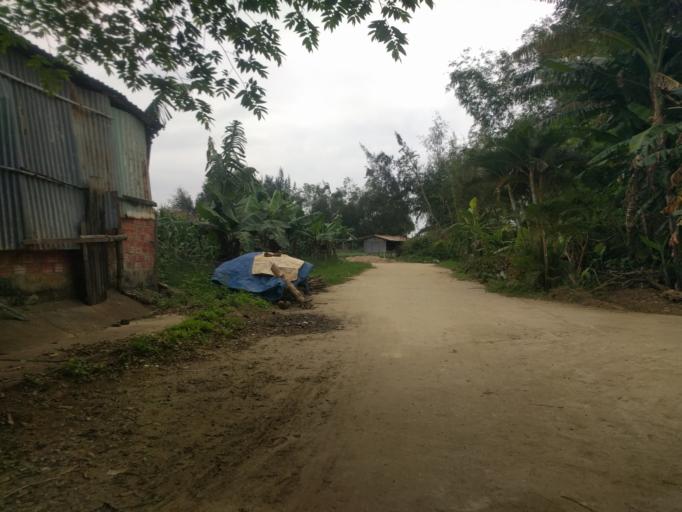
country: VN
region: Quang Nam
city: Hoi An
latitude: 15.8665
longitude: 108.3513
